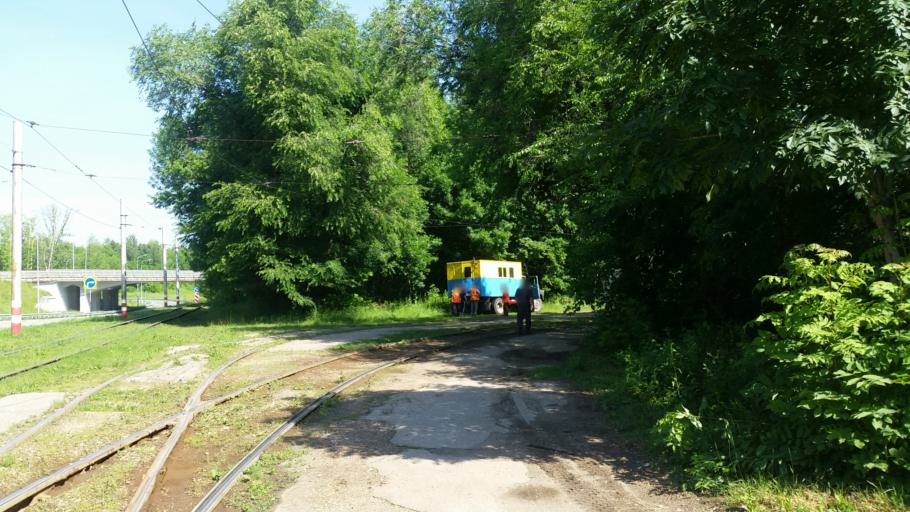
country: RU
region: Ulyanovsk
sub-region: Ulyanovskiy Rayon
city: Ulyanovsk
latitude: 54.3579
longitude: 48.3750
